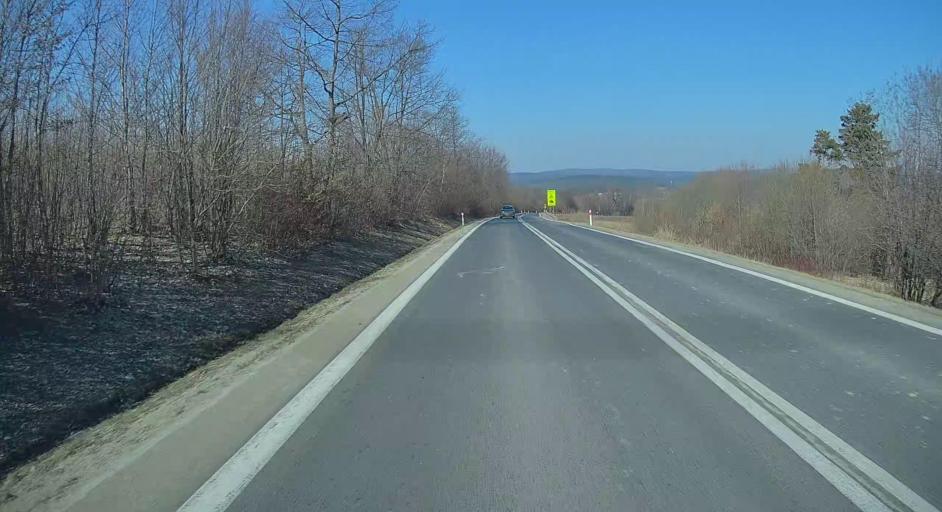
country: PL
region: Subcarpathian Voivodeship
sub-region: Powiat przemyski
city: Bircza
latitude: 49.6473
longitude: 22.4208
